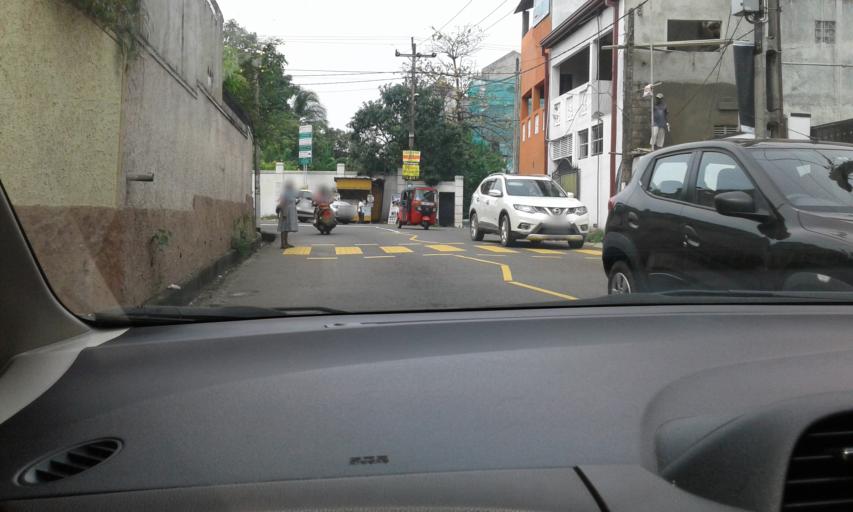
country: LK
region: Western
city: Sri Jayewardenepura Kotte
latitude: 6.8686
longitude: 79.9113
